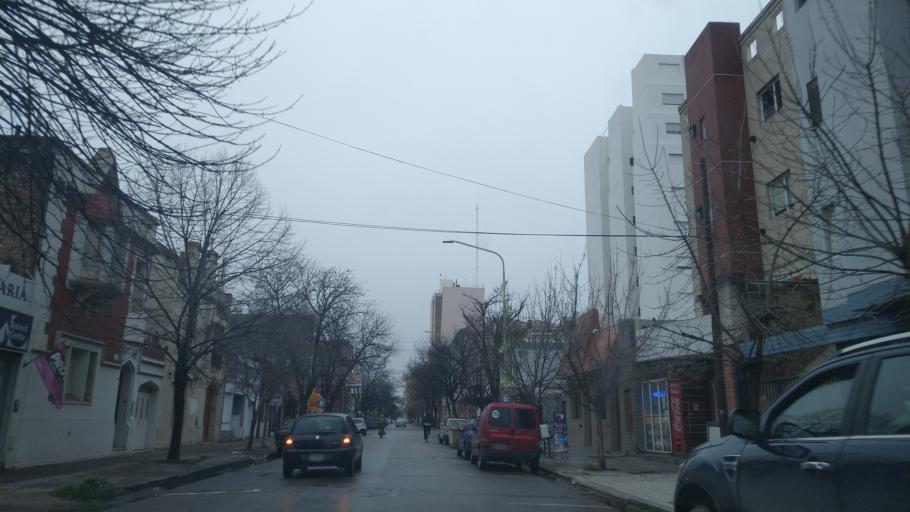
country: AR
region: Buenos Aires
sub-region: Partido de Bahia Blanca
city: Bahia Blanca
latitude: -38.7114
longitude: -62.2663
